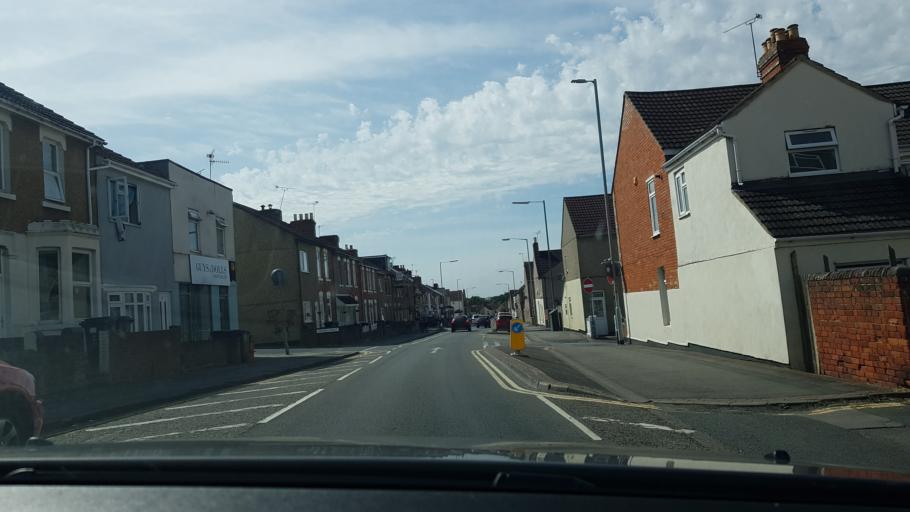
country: GB
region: England
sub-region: Borough of Swindon
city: Swindon
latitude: 51.5579
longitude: -1.7848
